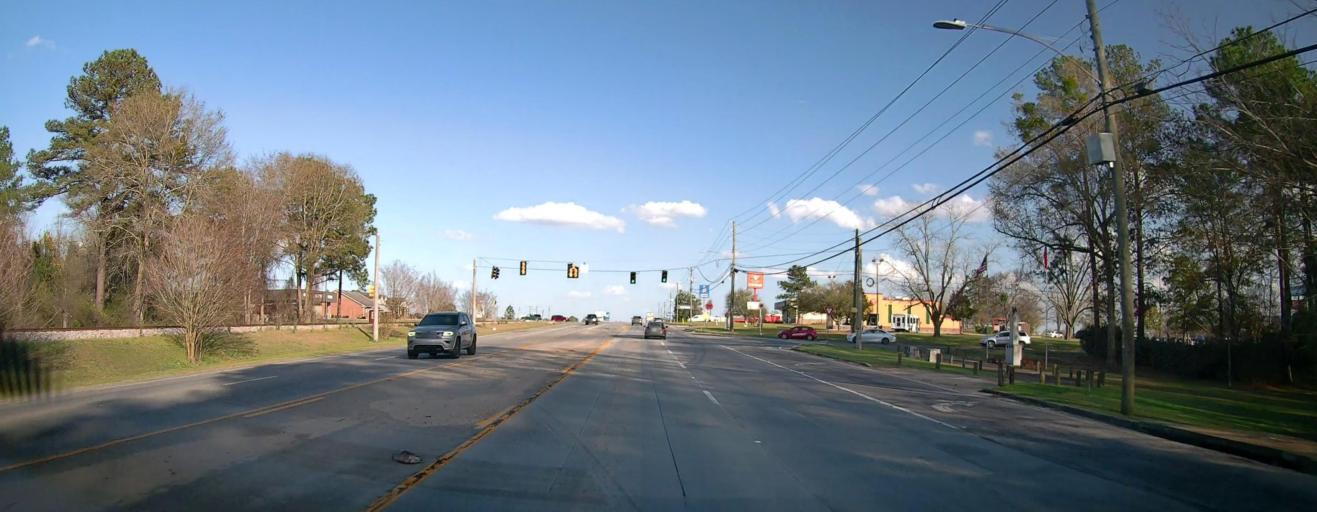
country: US
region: Georgia
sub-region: Toombs County
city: Lyons
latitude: 32.2051
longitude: -82.3639
